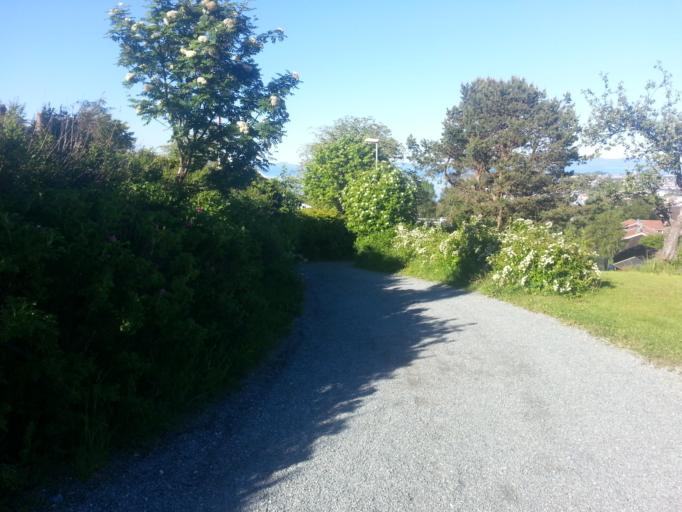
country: NO
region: Sor-Trondelag
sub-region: Trondheim
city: Trondheim
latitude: 63.4257
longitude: 10.3473
